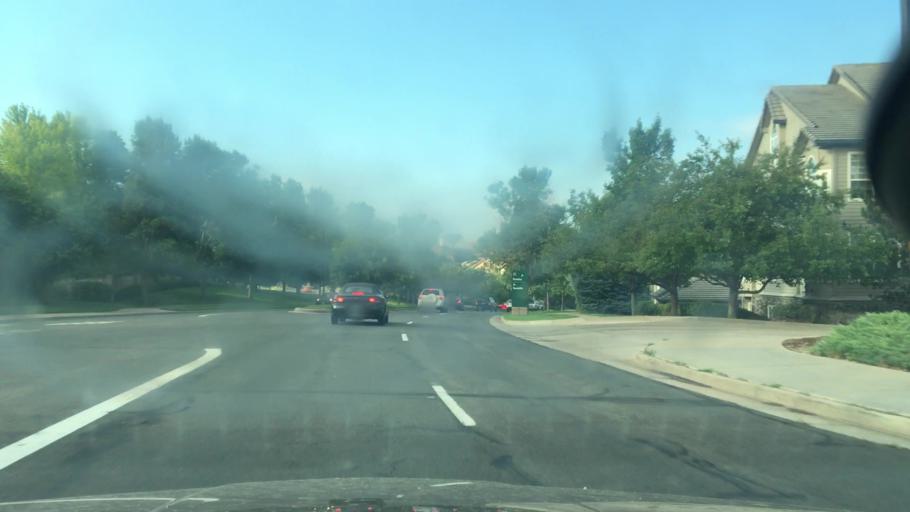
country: US
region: Colorado
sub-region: Arapahoe County
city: Castlewood
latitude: 39.6221
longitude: -104.8854
